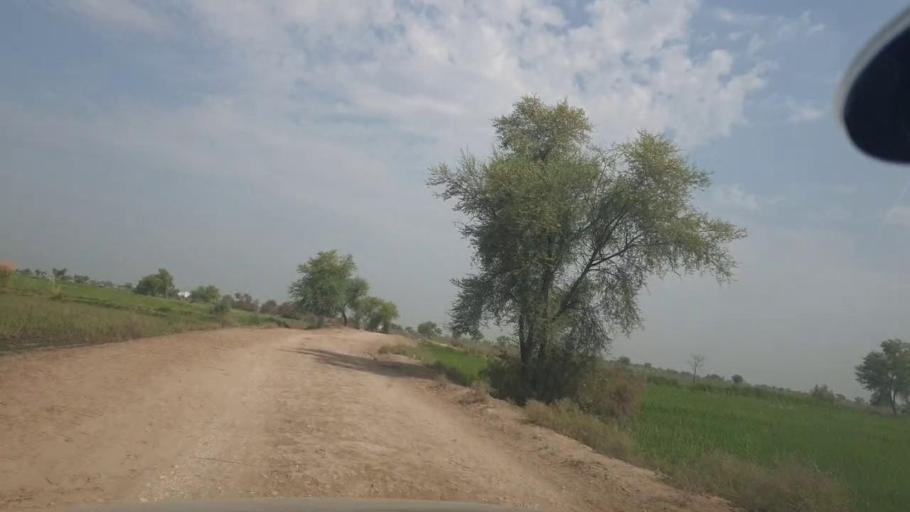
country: PK
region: Balochistan
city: Mehrabpur
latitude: 28.1224
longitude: 68.0907
